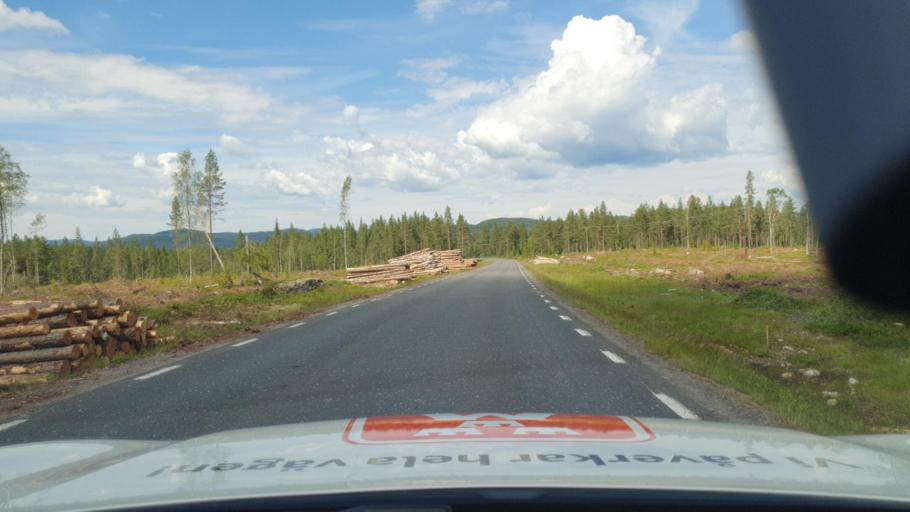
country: SE
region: Vaermland
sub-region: Torsby Kommun
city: Torsby
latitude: 60.5458
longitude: 12.7914
